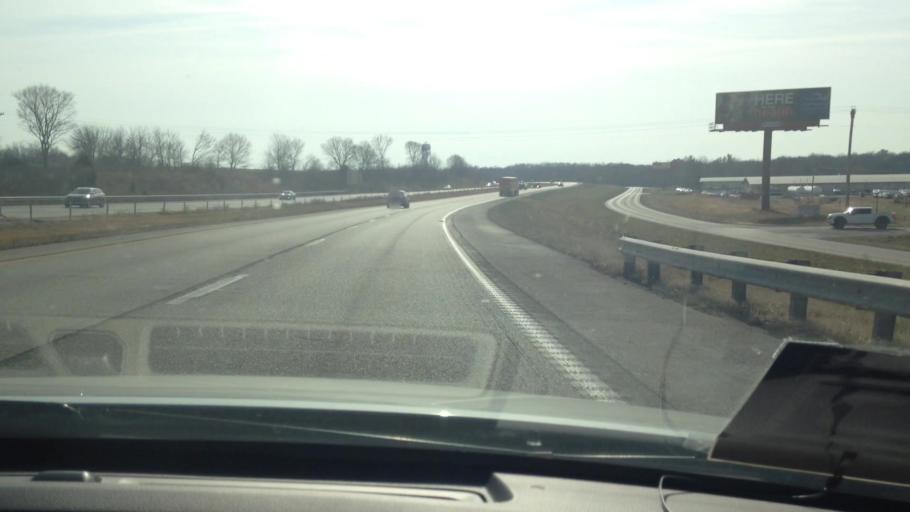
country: US
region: Missouri
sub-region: Cass County
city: Raymore
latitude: 38.7698
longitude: -94.4915
